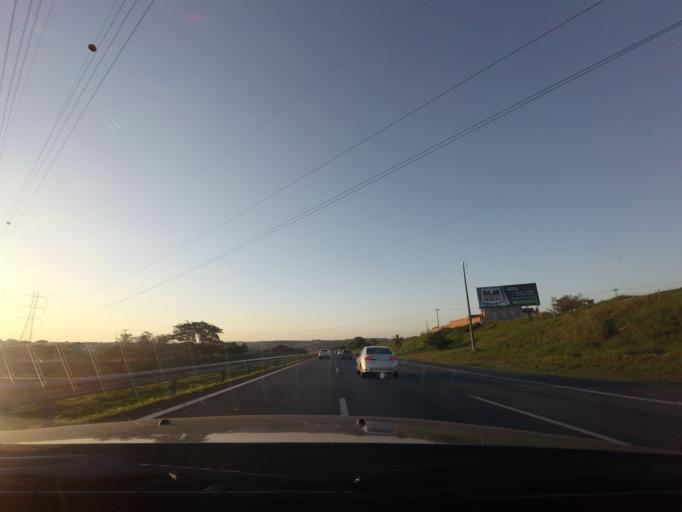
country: BR
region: Sao Paulo
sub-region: Campinas
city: Campinas
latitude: -22.9752
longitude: -47.1135
